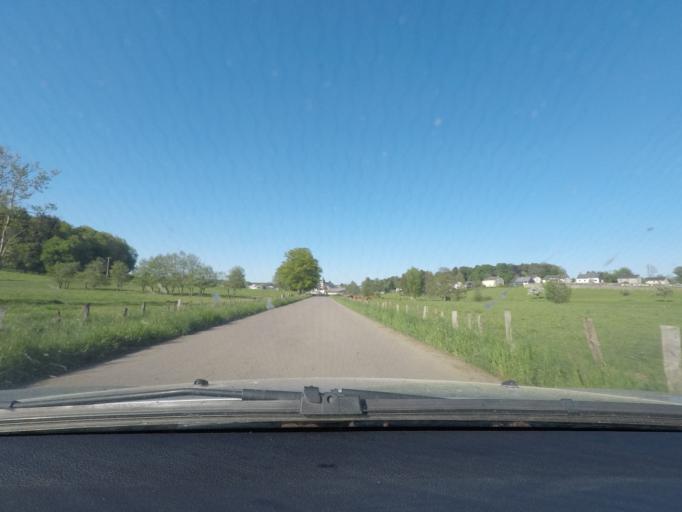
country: BE
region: Wallonia
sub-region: Province du Luxembourg
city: Tintigny
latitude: 49.7129
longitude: 5.4794
